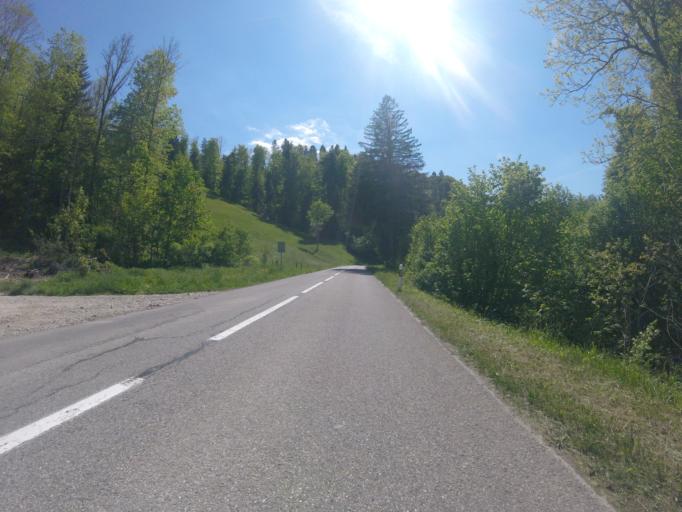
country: CH
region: Saint Gallen
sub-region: Wahlkreis Toggenburg
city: Mogelsberg
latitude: 47.3679
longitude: 9.1351
